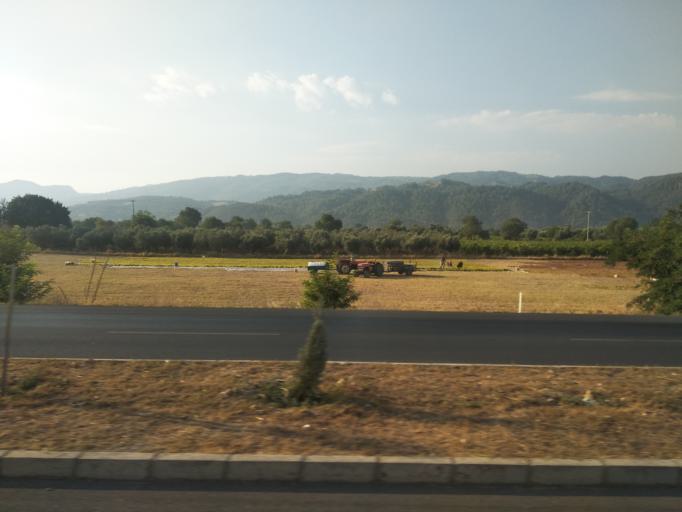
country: TR
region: Manisa
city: Ahmetli
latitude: 38.5046
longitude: 27.8810
